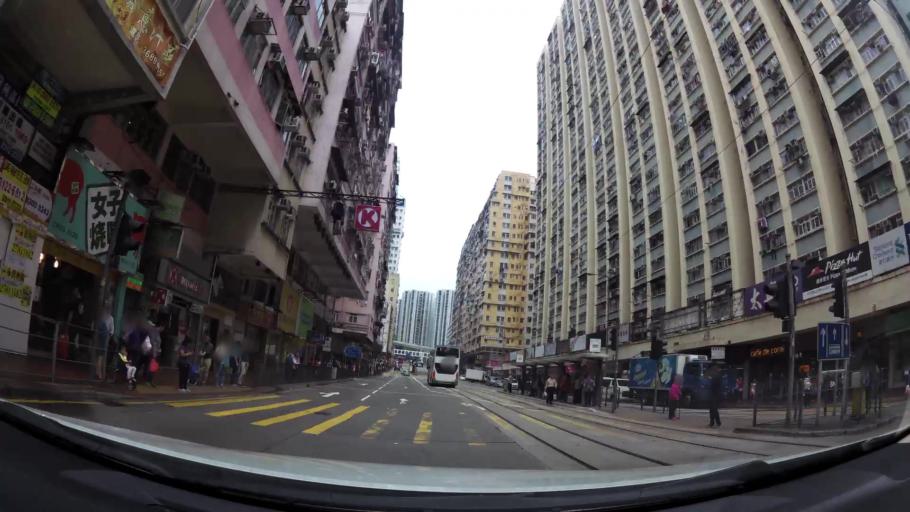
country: HK
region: Wanchai
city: Wan Chai
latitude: 22.2821
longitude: 114.2218
